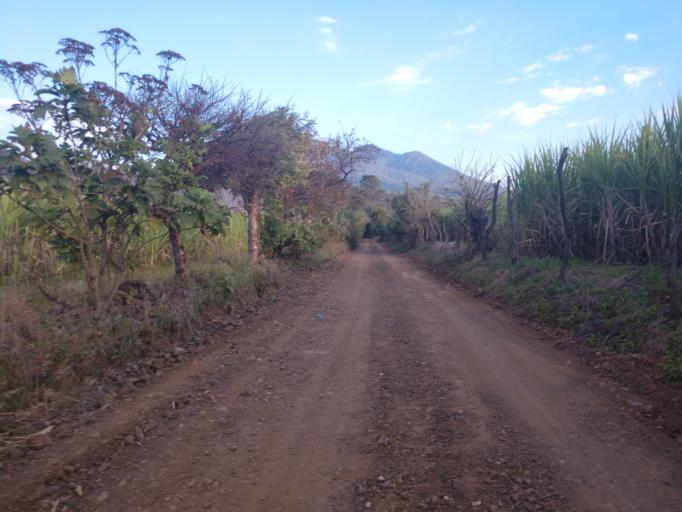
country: MX
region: Nayarit
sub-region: Tepic
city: La Corregidora
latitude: 21.4562
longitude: -104.7921
